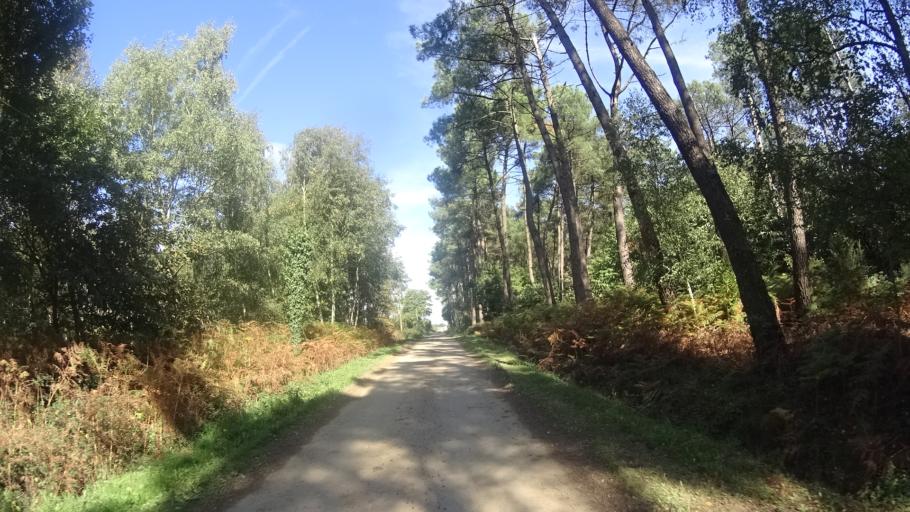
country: FR
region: Brittany
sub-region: Departement du Morbihan
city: La Gacilly
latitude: 47.7470
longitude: -2.1699
